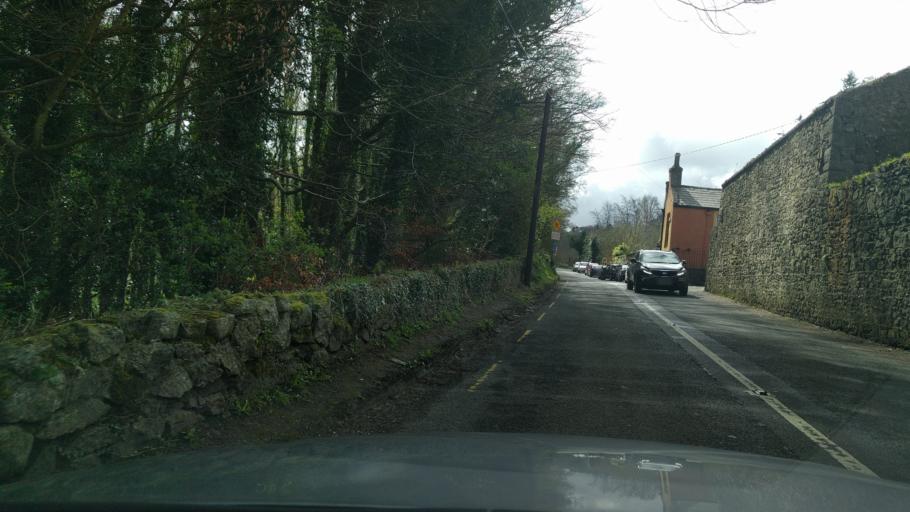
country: IE
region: Leinster
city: Ballyboden
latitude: 53.2540
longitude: -6.3209
